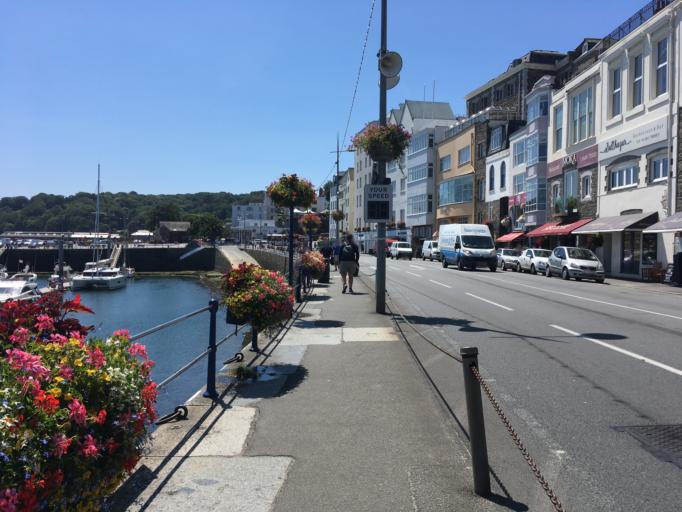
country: GG
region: St Peter Port
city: Saint Peter Port
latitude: 49.4560
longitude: -2.5356
